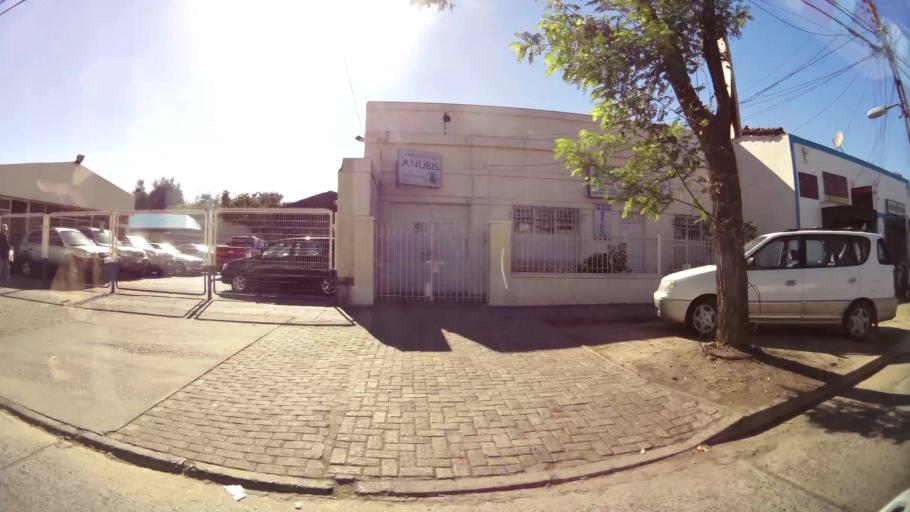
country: CL
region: O'Higgins
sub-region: Provincia de Cachapoal
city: Rancagua
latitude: -34.1732
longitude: -70.7470
